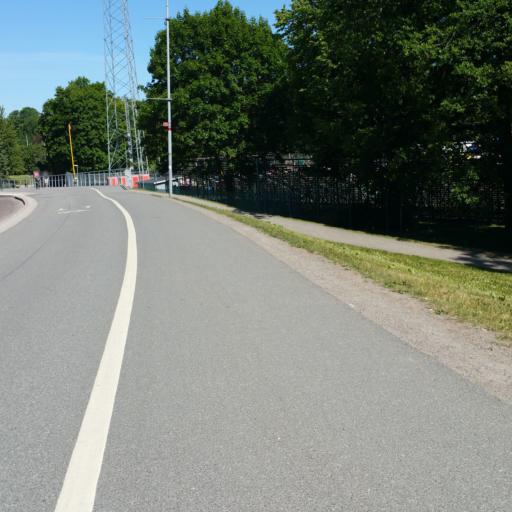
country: SE
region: Uppsala
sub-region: Uppsala Kommun
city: Uppsala
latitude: 59.8491
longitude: 17.6440
